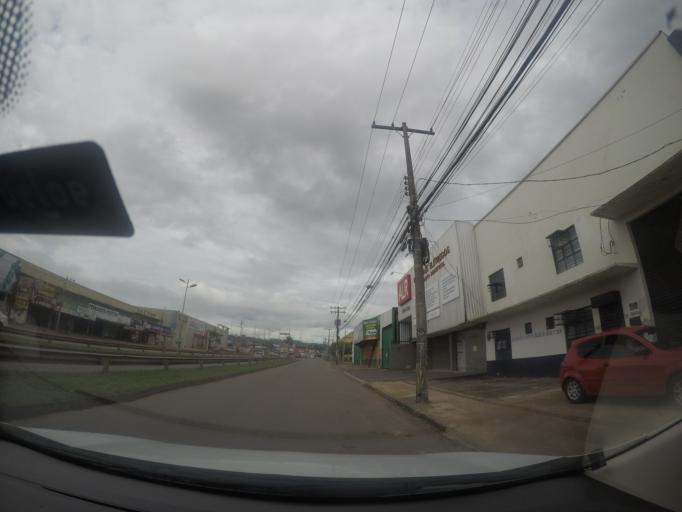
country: BR
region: Goias
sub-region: Goiania
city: Goiania
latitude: -16.6526
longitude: -49.3298
